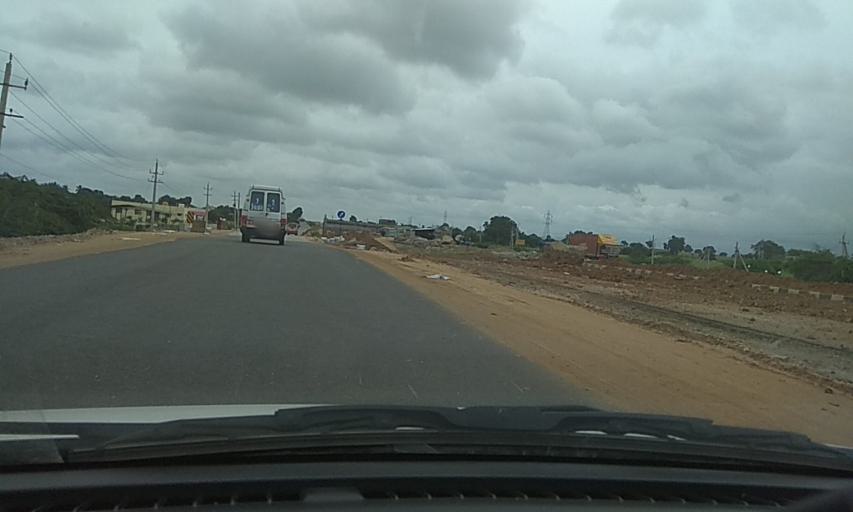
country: IN
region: Karnataka
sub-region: Chitradurga
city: Chitradurga
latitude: 14.2904
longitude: 76.2875
